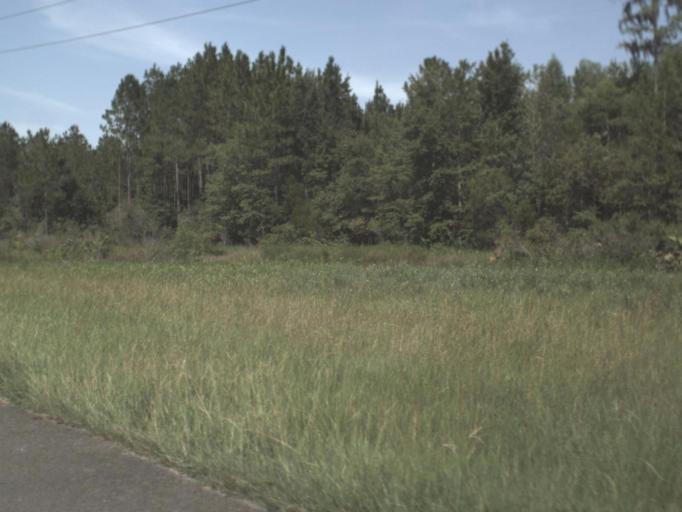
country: US
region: Florida
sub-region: Gilchrist County
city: Trenton
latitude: 29.6424
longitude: -82.7926
